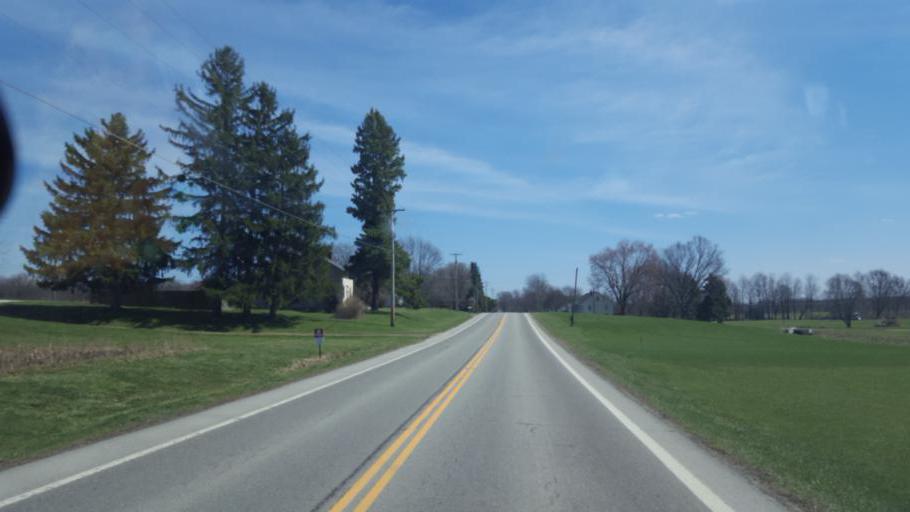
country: US
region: Ohio
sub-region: Ashland County
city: Ashland
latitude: 40.8828
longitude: -82.3672
